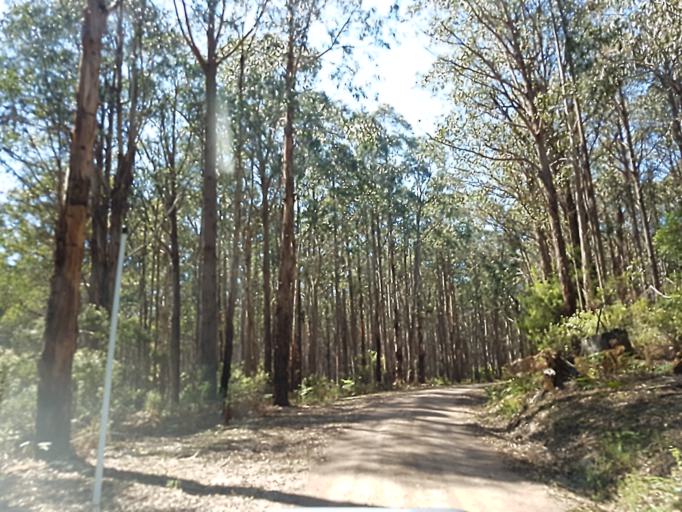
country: AU
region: Victoria
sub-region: East Gippsland
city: Lakes Entrance
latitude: -37.2893
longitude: 148.3123
